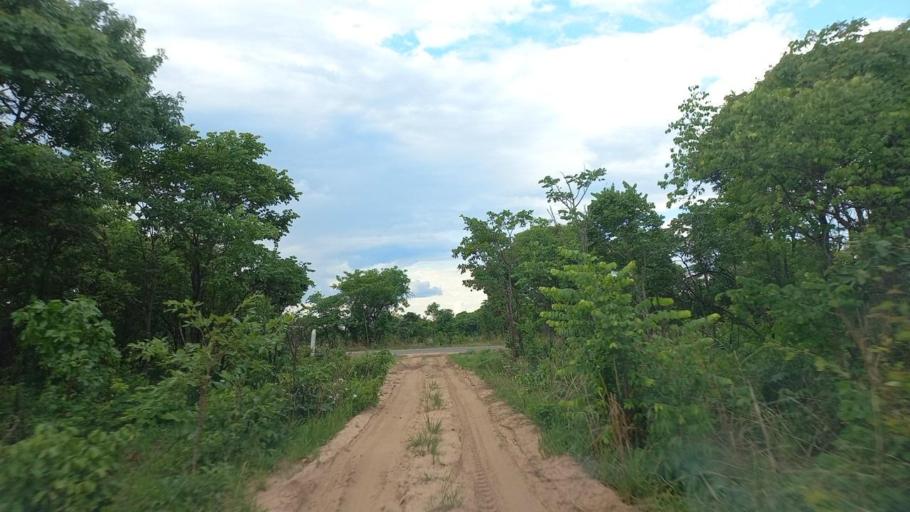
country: ZM
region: North-Western
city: Kabompo
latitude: -13.2401
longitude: 24.5345
